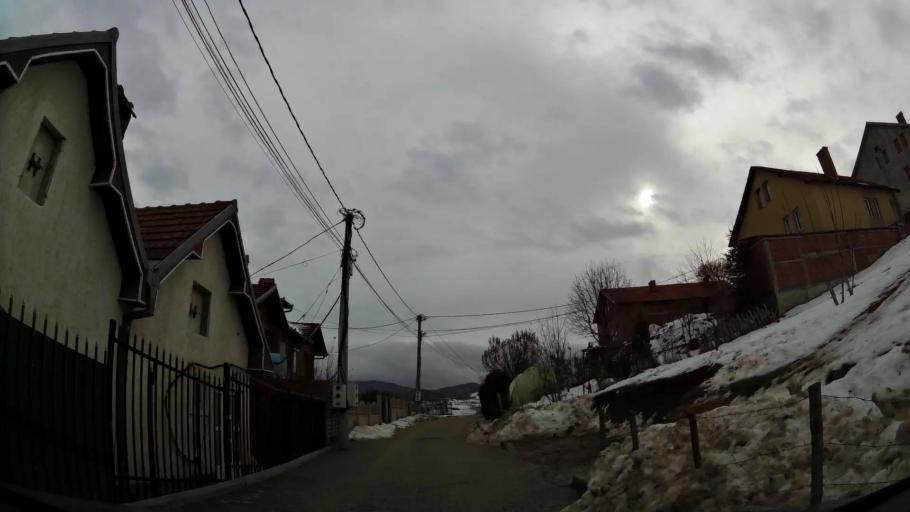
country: XK
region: Pristina
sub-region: Komuna e Prishtines
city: Pristina
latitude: 42.6900
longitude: 21.1753
